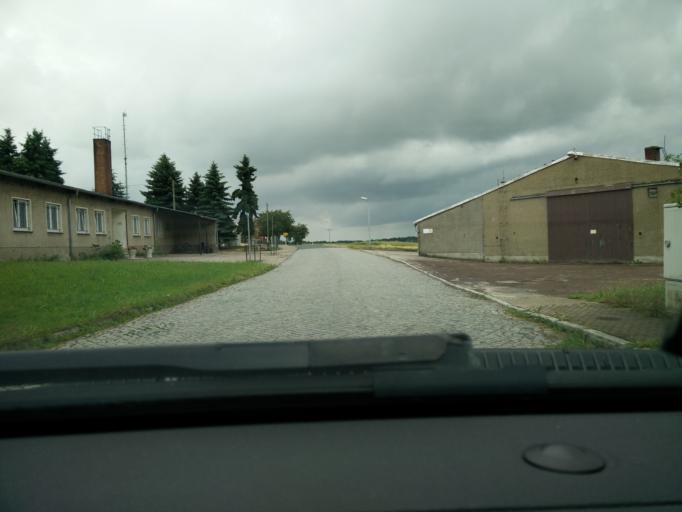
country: DE
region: Saxony
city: Bad Lausick
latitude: 51.1400
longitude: 12.6879
